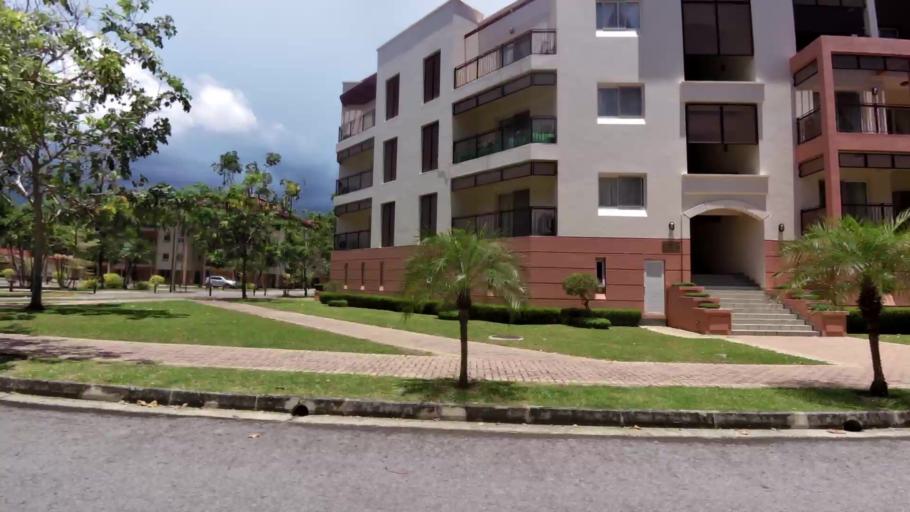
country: BN
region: Brunei and Muara
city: Bandar Seri Begawan
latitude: 4.9529
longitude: 114.8938
